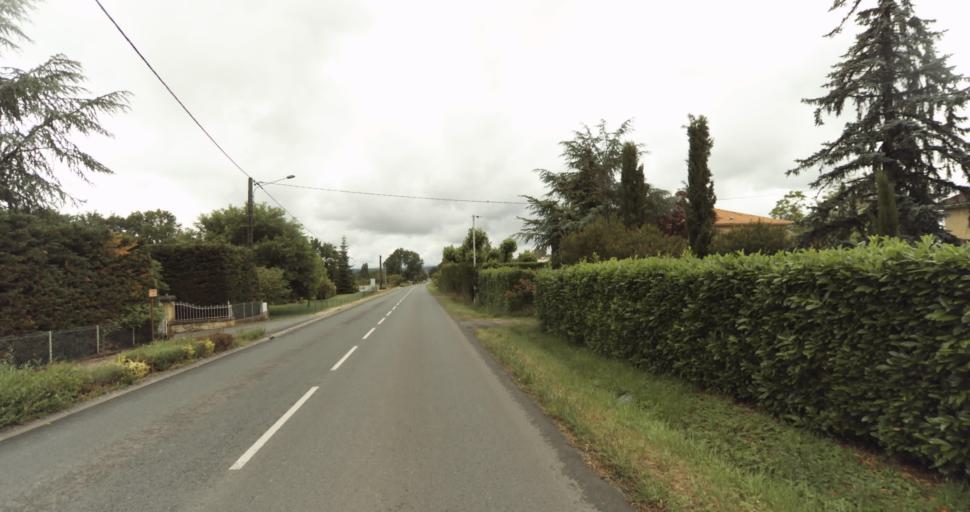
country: FR
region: Aquitaine
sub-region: Departement de la Dordogne
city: Beaumont-du-Perigord
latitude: 44.7561
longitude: 0.7726
